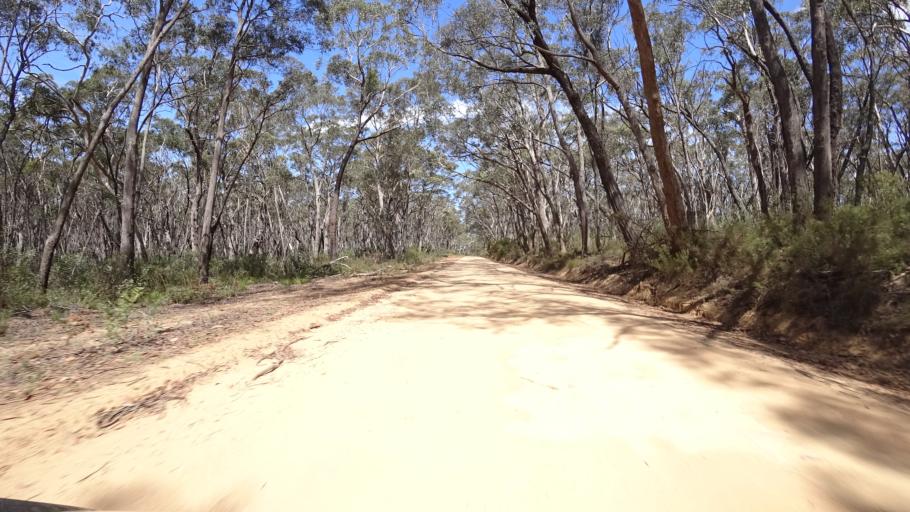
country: AU
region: New South Wales
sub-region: Lithgow
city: Lithgow
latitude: -33.3073
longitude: 150.2398
